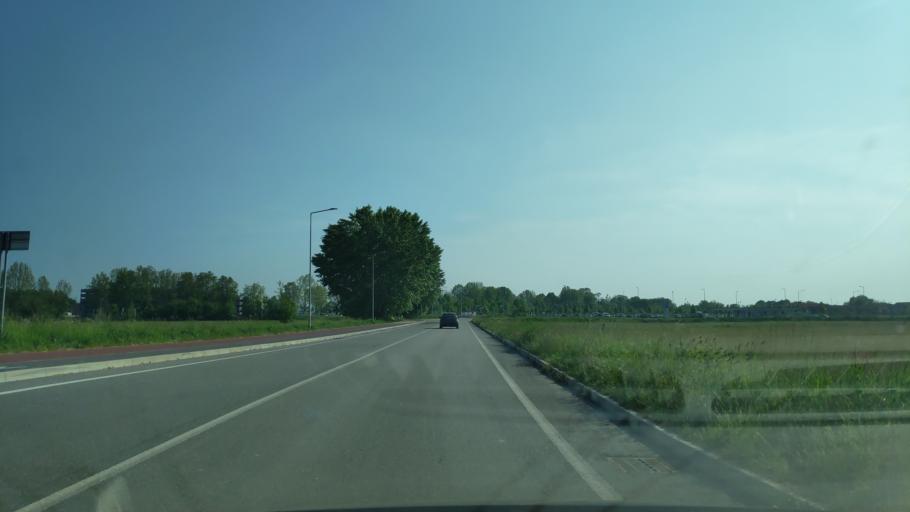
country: IT
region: Lombardy
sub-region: Citta metropolitana di Milano
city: Novegro-Tregarezzo-San Felice
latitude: 45.4678
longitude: 9.2777
